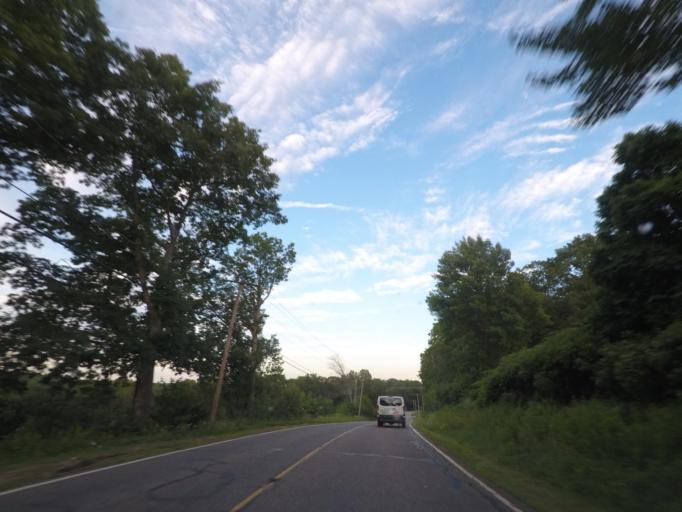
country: US
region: Massachusetts
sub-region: Worcester County
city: Warren
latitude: 42.1727
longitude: -72.1542
